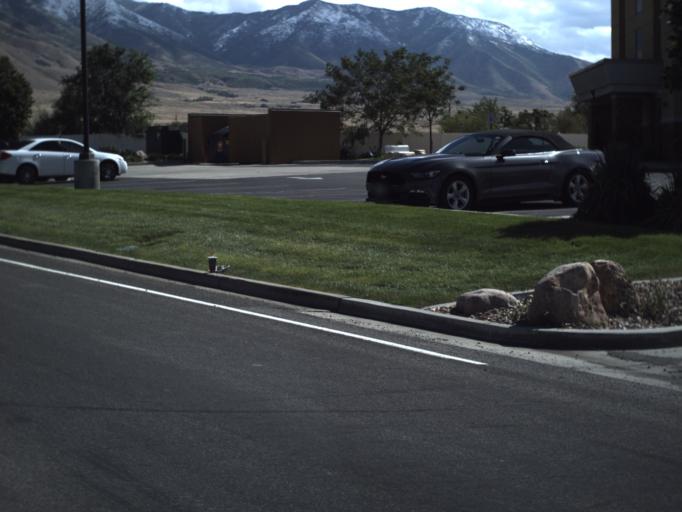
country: US
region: Utah
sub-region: Tooele County
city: Stansbury park
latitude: 40.6855
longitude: -112.2678
